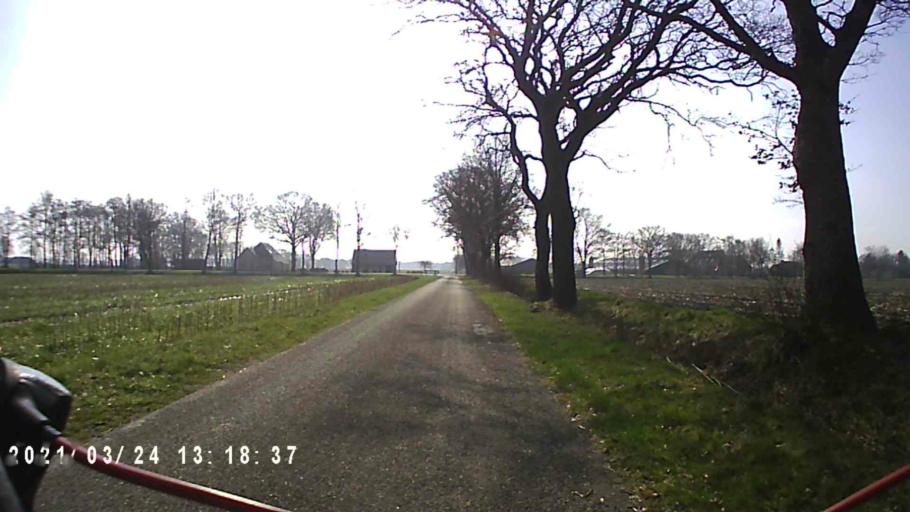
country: NL
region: Groningen
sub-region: Gemeente Leek
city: Leek
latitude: 53.1059
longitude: 6.2932
